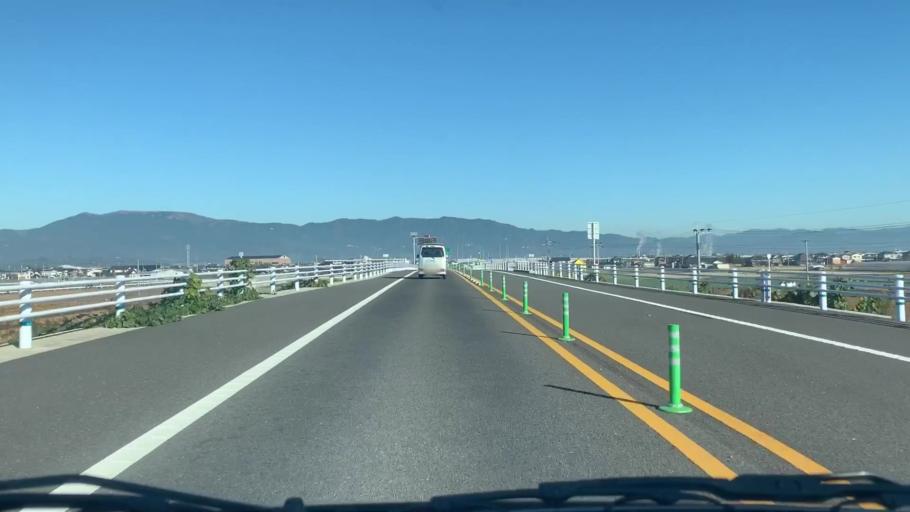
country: JP
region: Saga Prefecture
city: Saga-shi
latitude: 33.2142
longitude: 130.2145
